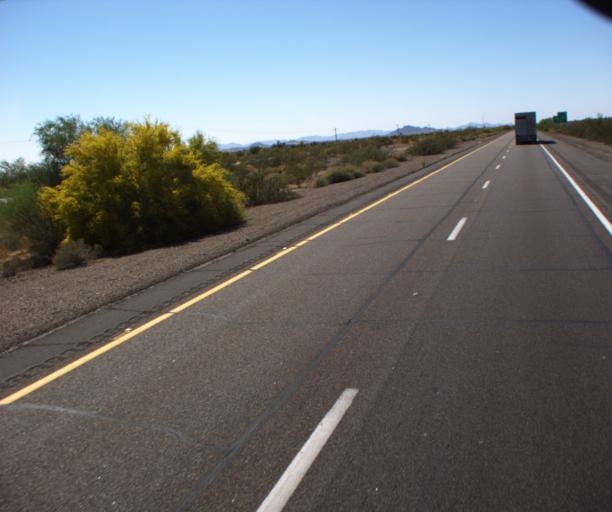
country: US
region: Arizona
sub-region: Maricopa County
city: Gila Bend
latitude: 32.8387
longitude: -113.3352
